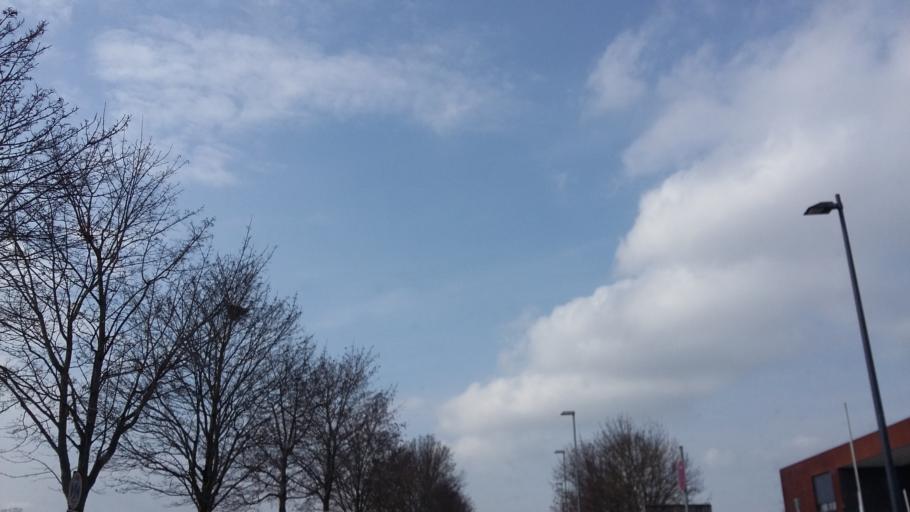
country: DE
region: Bavaria
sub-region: Upper Bavaria
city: Garching bei Munchen
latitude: 48.2677
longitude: 11.6647
